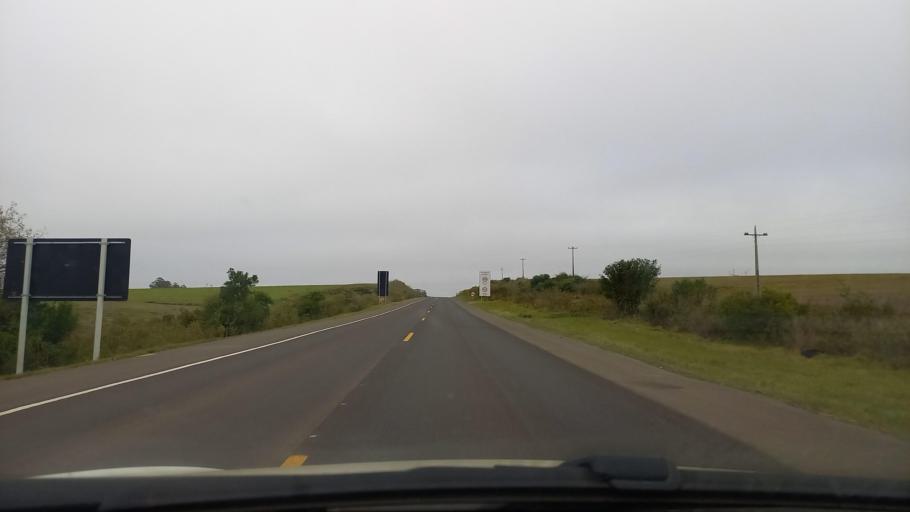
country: BR
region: Rio Grande do Sul
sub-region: Rosario Do Sul
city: Rosario do Sul
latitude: -30.2854
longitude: -54.9834
